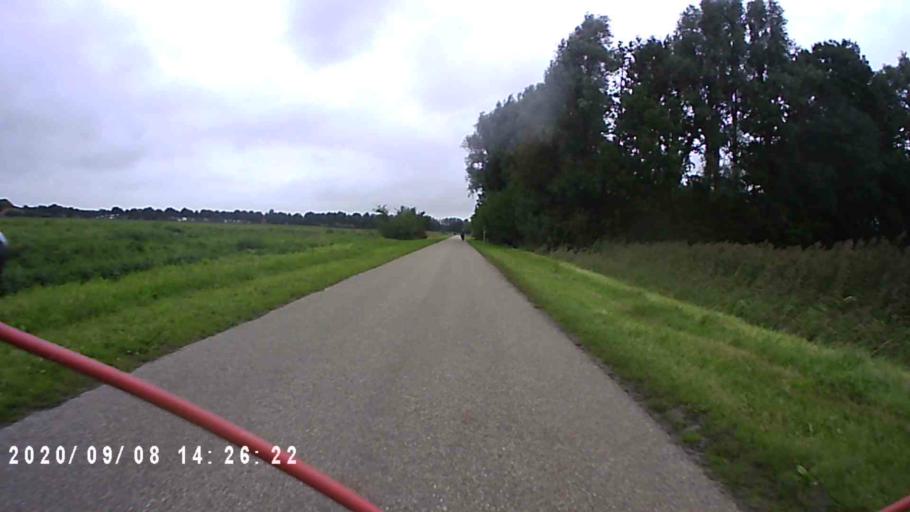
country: NL
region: Groningen
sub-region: Gemeente Slochteren
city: Slochteren
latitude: 53.2203
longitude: 6.8225
